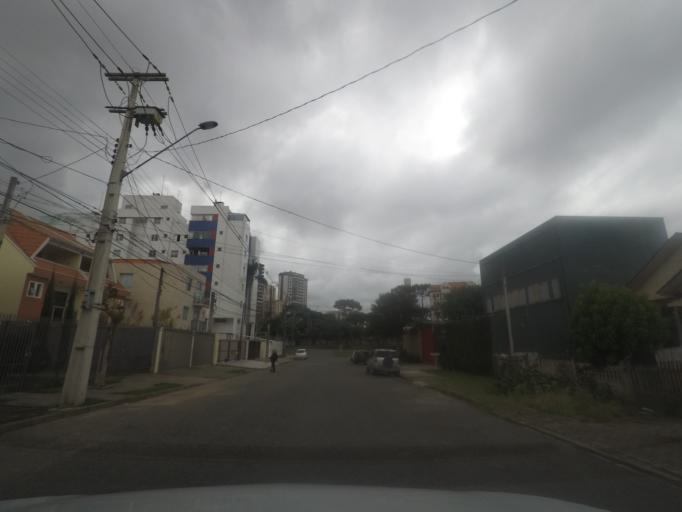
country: BR
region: Parana
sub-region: Curitiba
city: Curitiba
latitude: -25.4368
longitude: -49.2483
